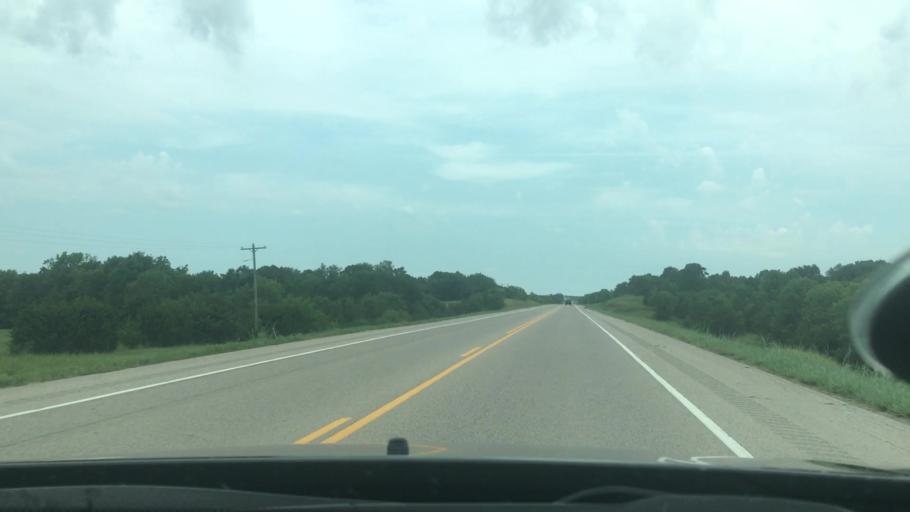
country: US
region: Oklahoma
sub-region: Seminole County
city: Konawa
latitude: 34.9955
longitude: -96.6791
